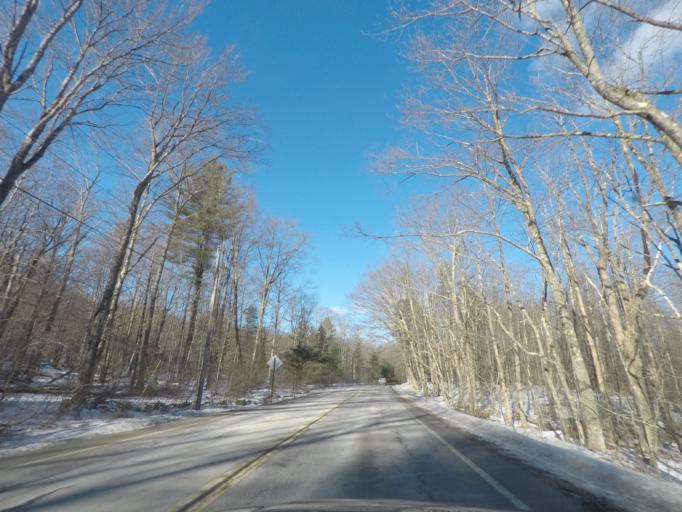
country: US
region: Massachusetts
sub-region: Berkshire County
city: West Stockbridge
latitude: 42.3236
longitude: -73.4712
